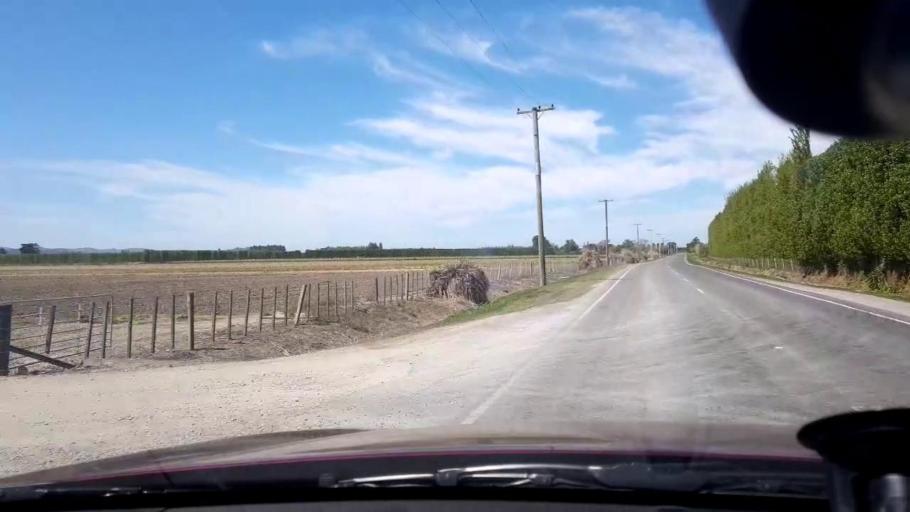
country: NZ
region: Gisborne
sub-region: Gisborne District
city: Gisborne
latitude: -38.6297
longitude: 177.9265
